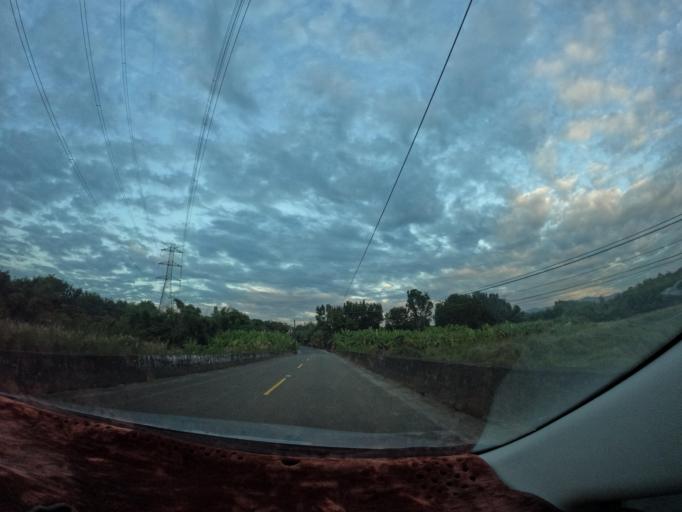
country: TW
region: Taiwan
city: Yujing
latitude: 23.0356
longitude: 120.4169
